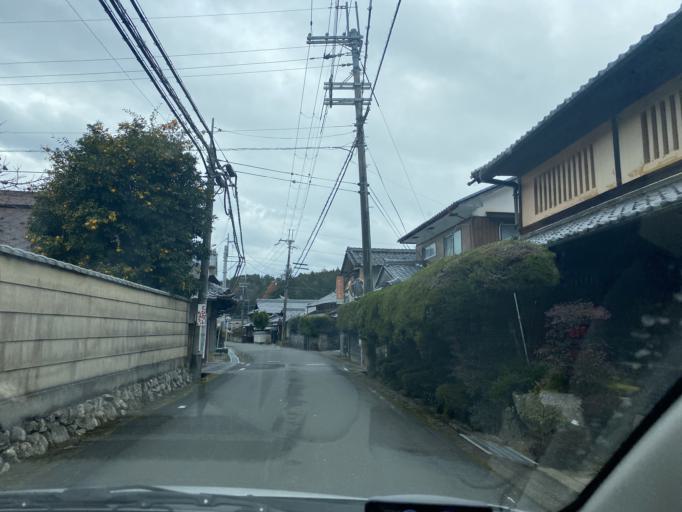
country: JP
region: Kyoto
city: Kameoka
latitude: 35.0581
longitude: 135.4465
